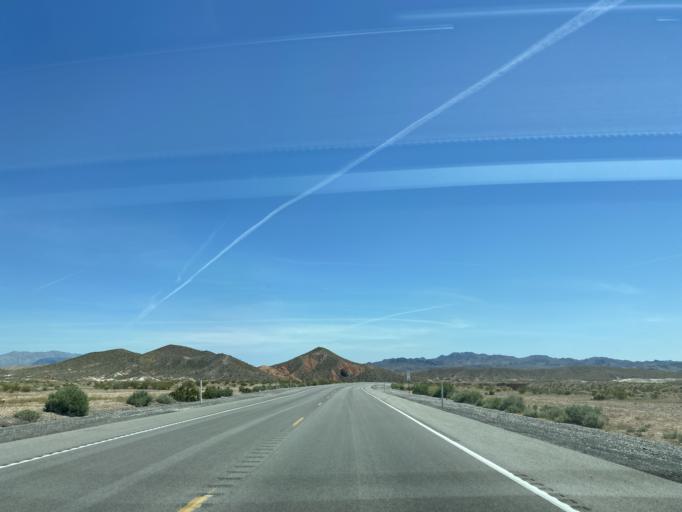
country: US
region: Nevada
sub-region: Clark County
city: Henderson
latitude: 36.1783
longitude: -114.9150
